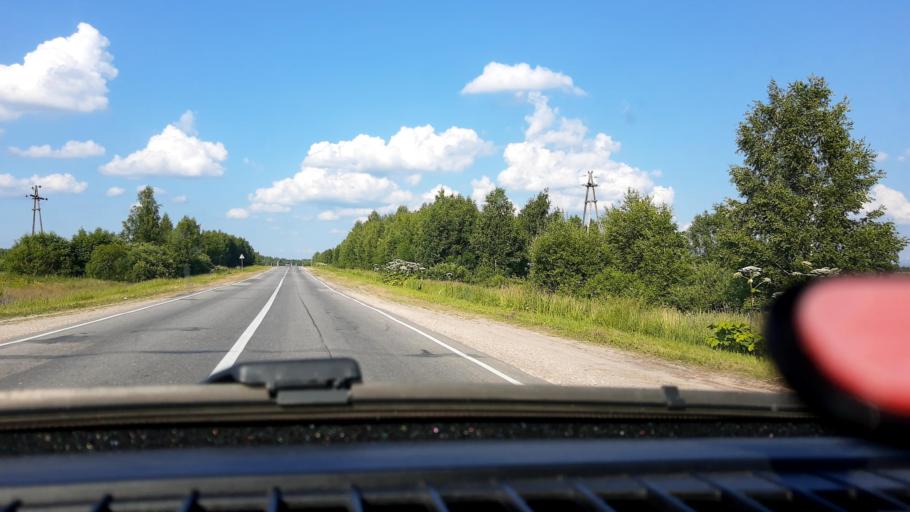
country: RU
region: Nizjnij Novgorod
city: Sitniki
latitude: 56.4968
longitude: 44.0147
